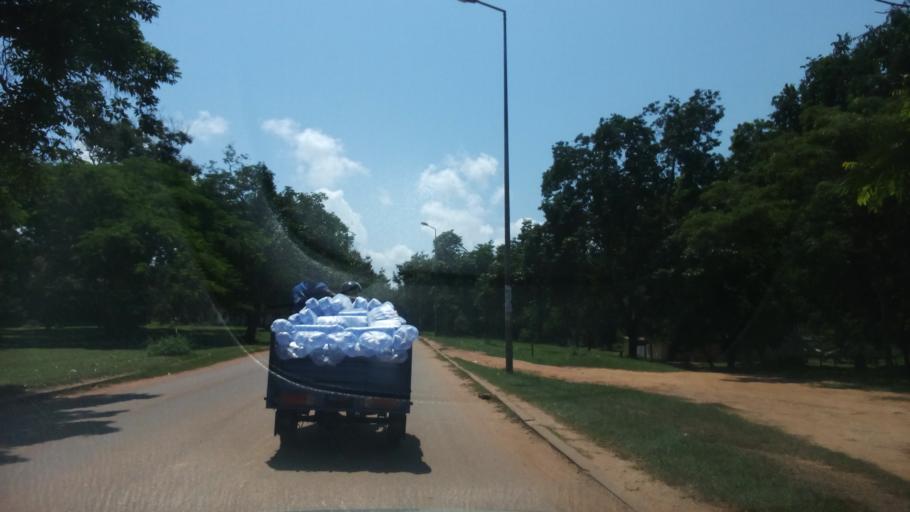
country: GH
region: Central
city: Cape Coast
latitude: 5.1228
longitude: -1.2916
